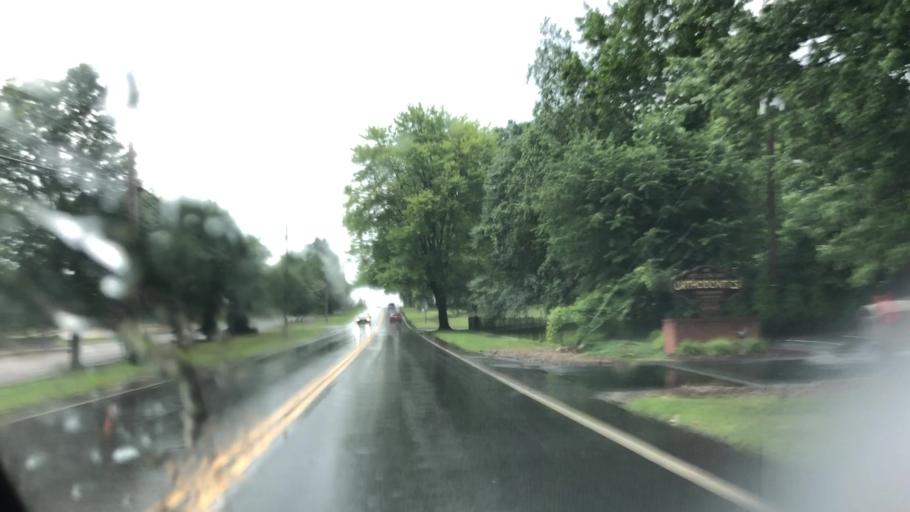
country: US
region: Ohio
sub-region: Stark County
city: Massillon
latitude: 40.8285
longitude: -81.5027
